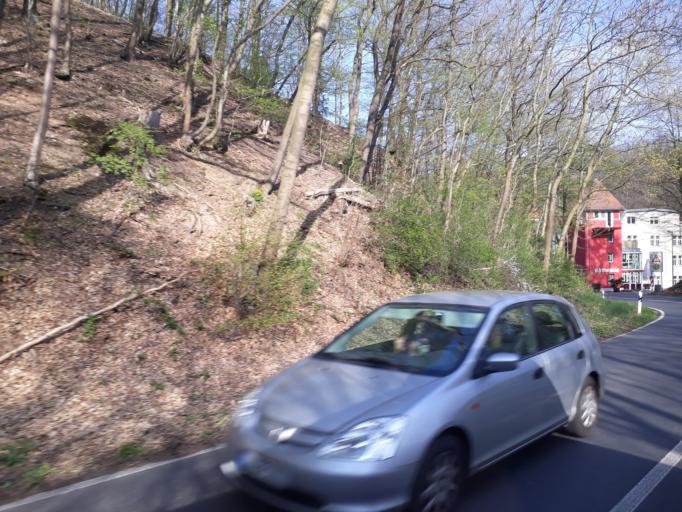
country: DE
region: Saxony
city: Kreischa
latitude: 50.9750
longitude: 13.7838
